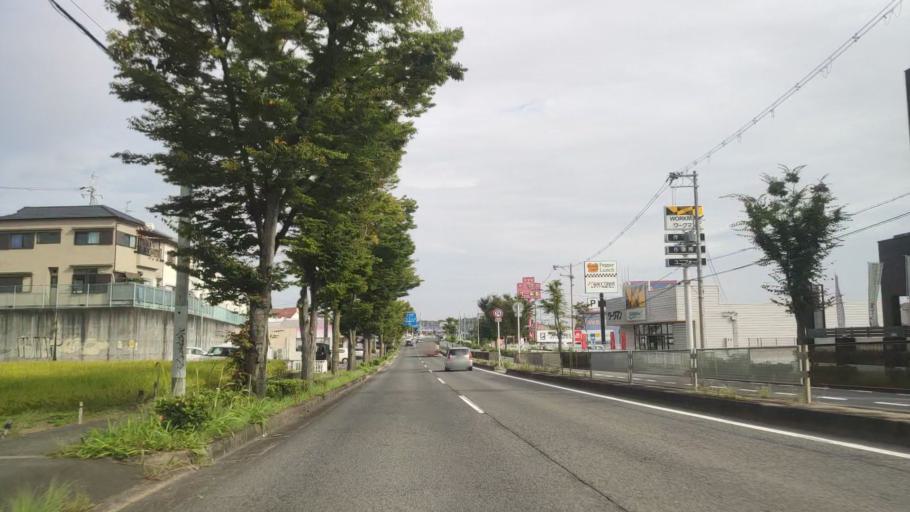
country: JP
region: Osaka
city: Tondabayashicho
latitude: 34.4646
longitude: 135.5752
